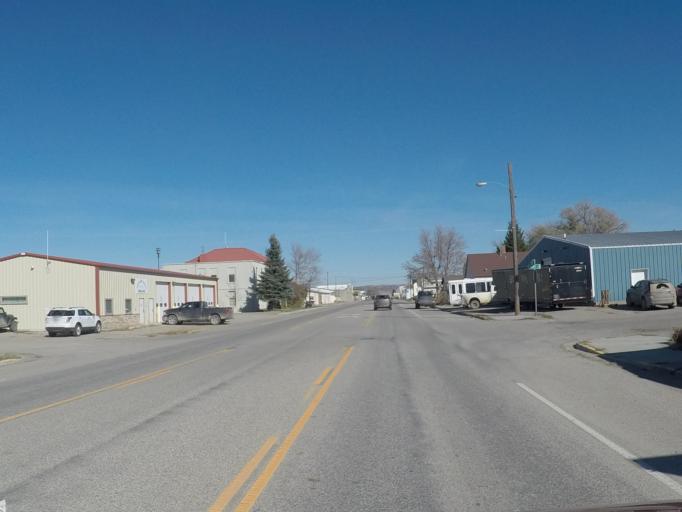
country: US
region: Montana
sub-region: Sweet Grass County
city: Big Timber
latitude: 45.8334
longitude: -109.9579
